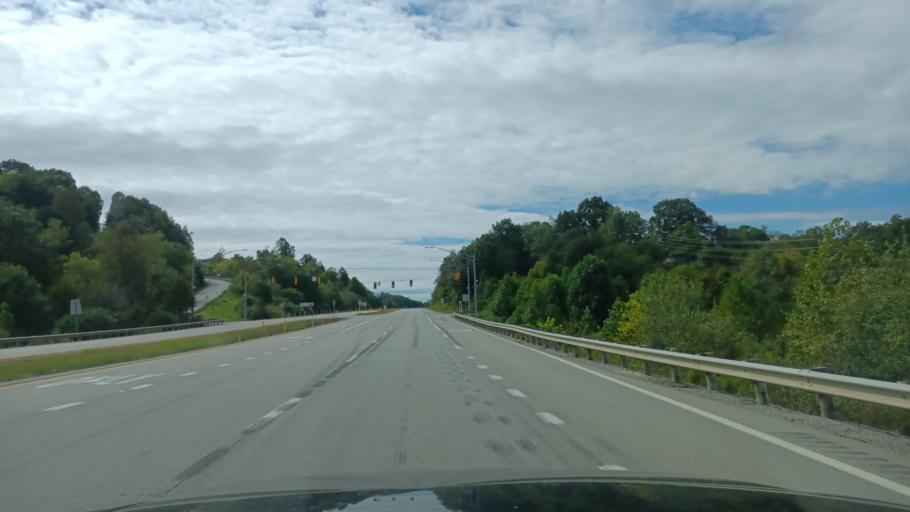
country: US
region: West Virginia
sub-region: Ritchie County
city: Pennsboro
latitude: 39.2735
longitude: -80.8871
